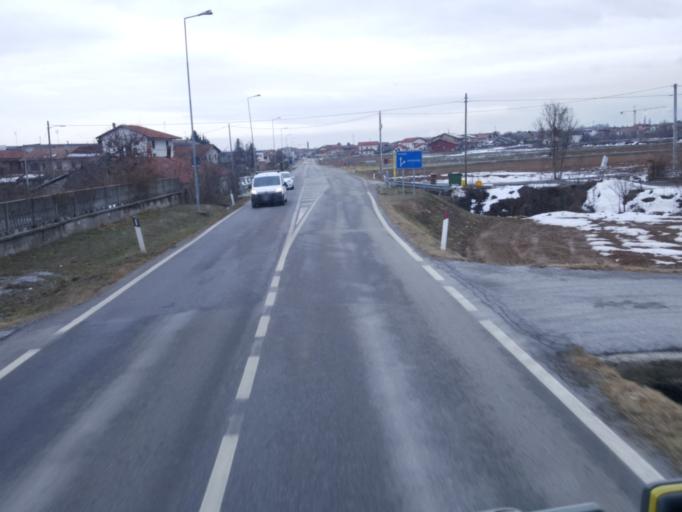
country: IT
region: Piedmont
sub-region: Provincia di Cuneo
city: San Rocco
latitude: 44.3989
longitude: 7.4629
